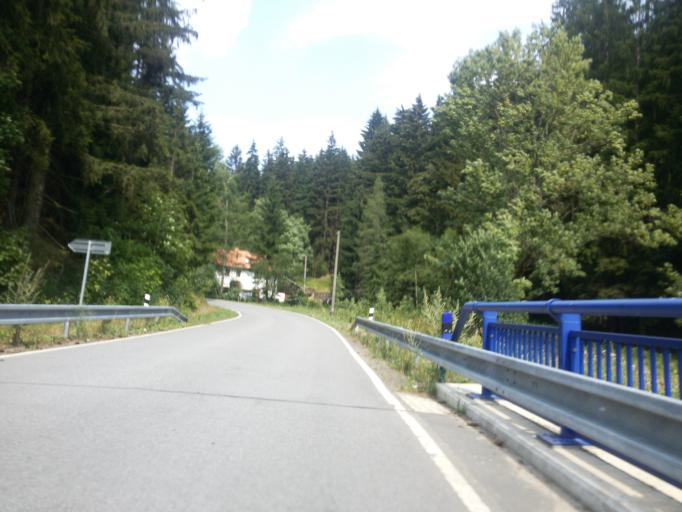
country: CZ
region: South Moravian
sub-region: Okres Brno-Venkov
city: Lomnice
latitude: 49.4551
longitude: 16.4363
